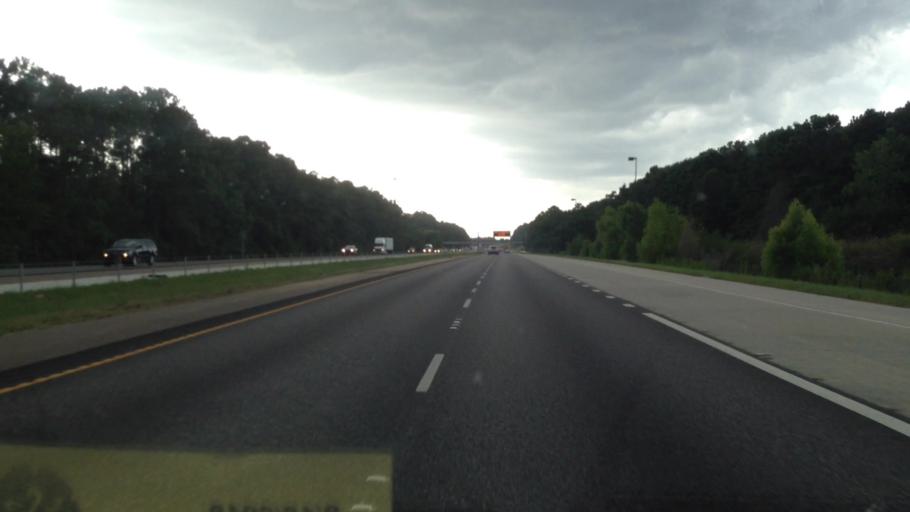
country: US
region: Louisiana
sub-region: Saint Tammany Parish
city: Slidell
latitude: 30.2994
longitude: -89.7165
